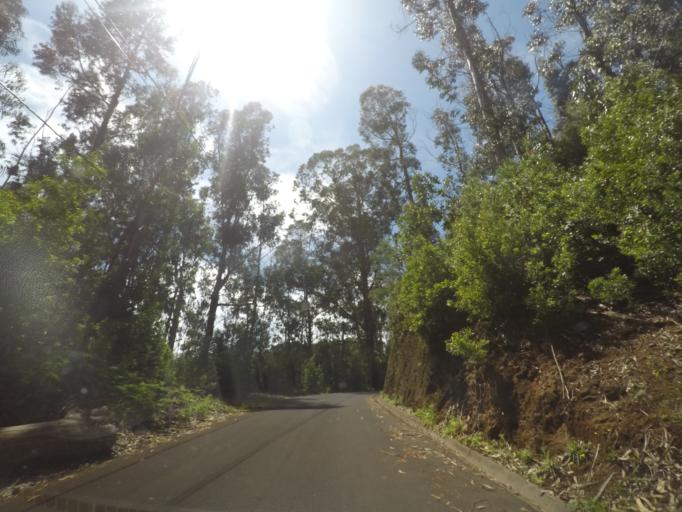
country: PT
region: Madeira
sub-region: Calheta
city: Arco da Calheta
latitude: 32.7274
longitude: -17.1323
